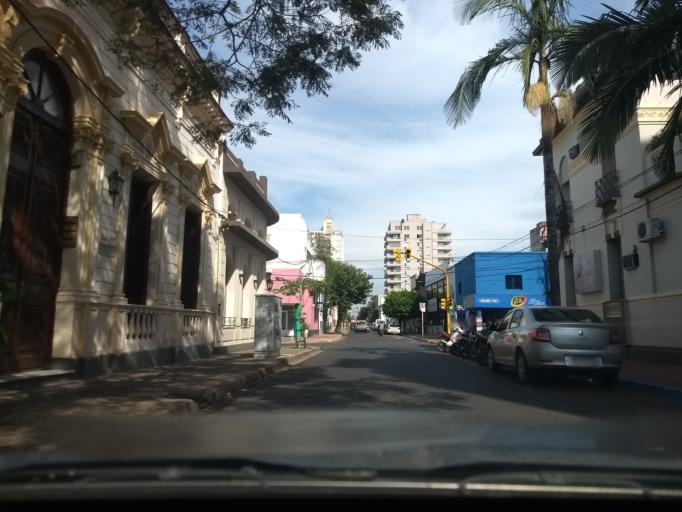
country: AR
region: Corrientes
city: Corrientes
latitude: -27.4656
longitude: -58.8302
